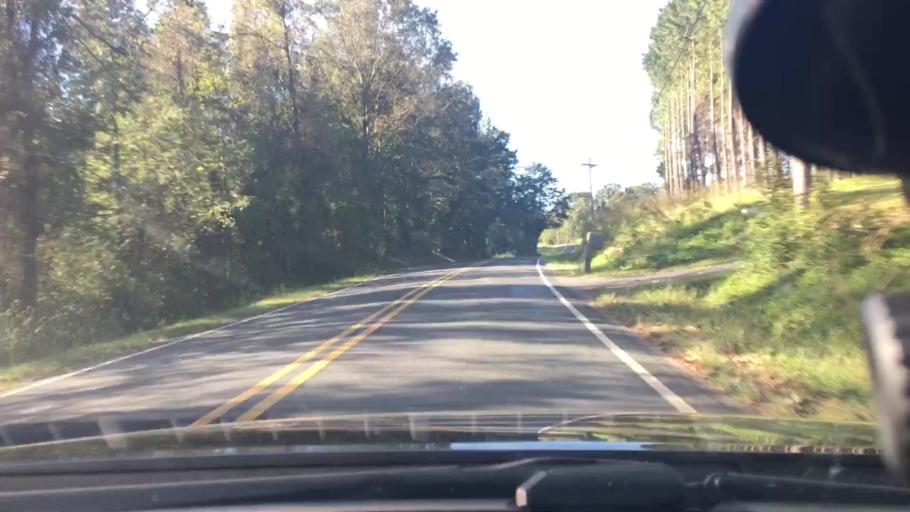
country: US
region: North Carolina
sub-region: Stanly County
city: Badin
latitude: 35.3525
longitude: -80.1180
